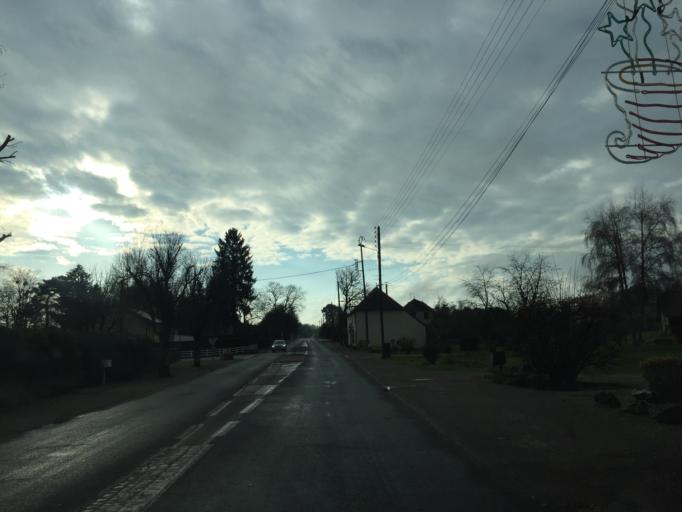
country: FR
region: Franche-Comte
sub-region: Departement du Jura
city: Mont-sous-Vaudrey
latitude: 46.9751
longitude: 5.6040
